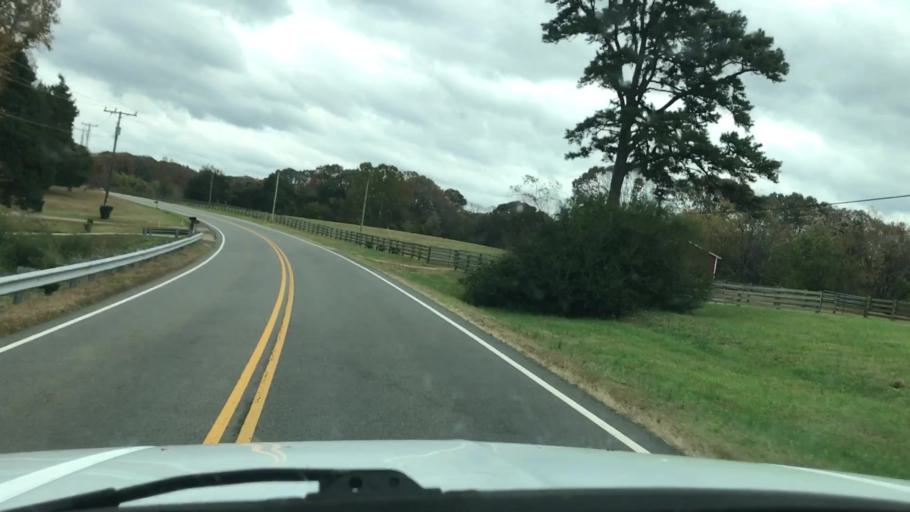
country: US
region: Virginia
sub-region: Goochland County
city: Goochland
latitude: 37.6382
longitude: -77.8126
